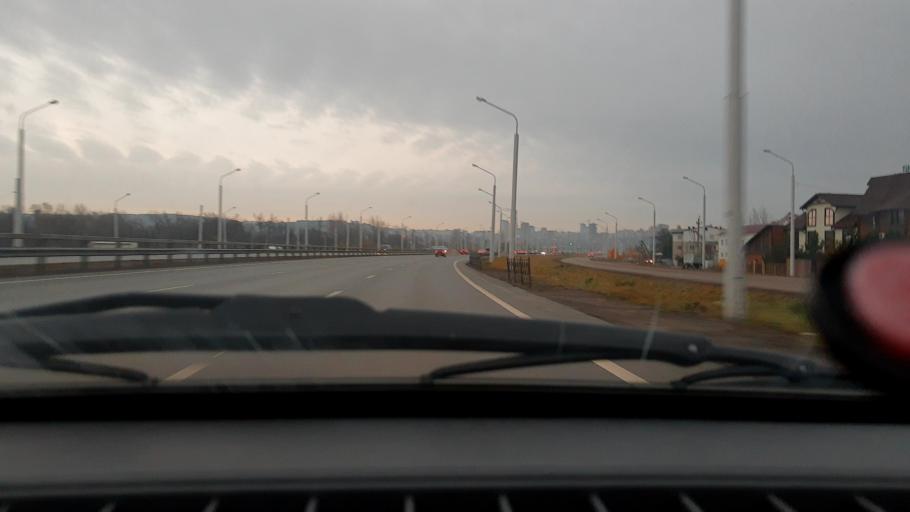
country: RU
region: Bashkortostan
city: Ufa
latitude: 54.7740
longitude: 55.9521
